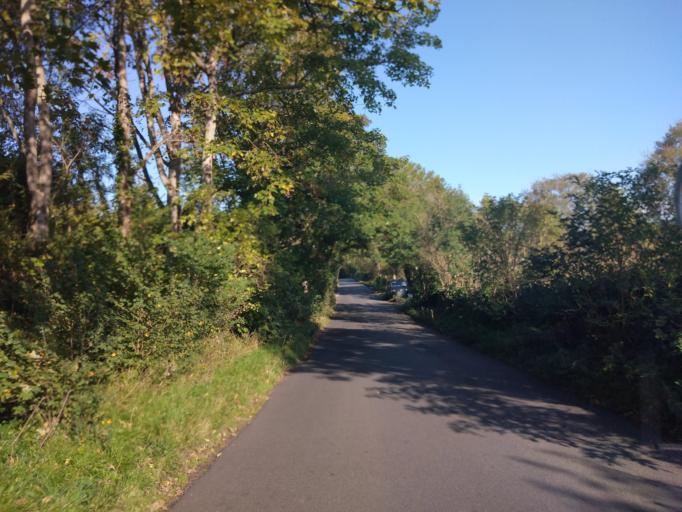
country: GB
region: England
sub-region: East Sussex
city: Seaford
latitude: 50.7984
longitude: 0.1527
